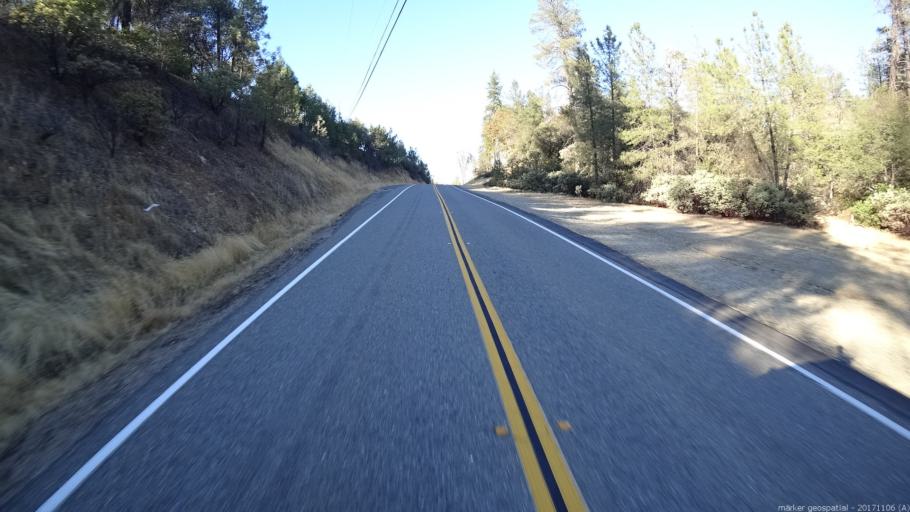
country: US
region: California
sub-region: Shasta County
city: Shasta
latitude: 40.5796
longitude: -122.4810
